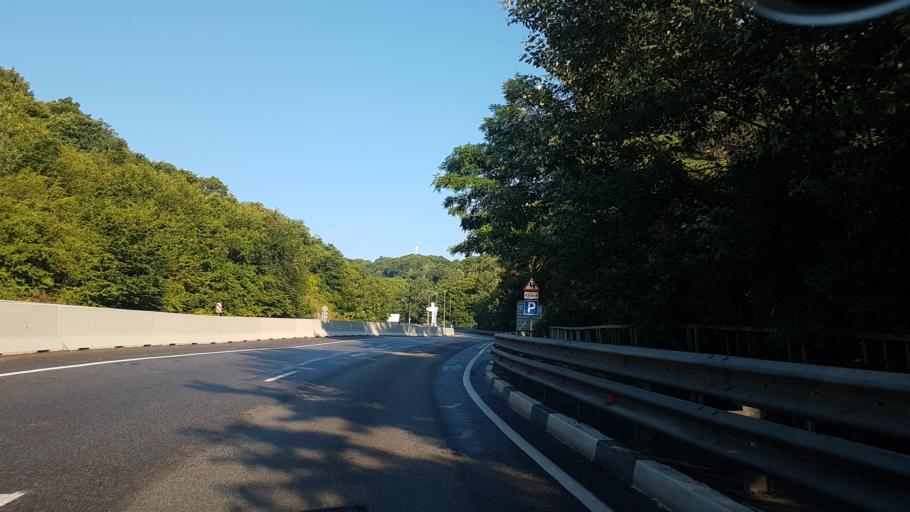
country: RU
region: Krasnodarskiy
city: Dagomys
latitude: 43.6441
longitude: 39.6995
